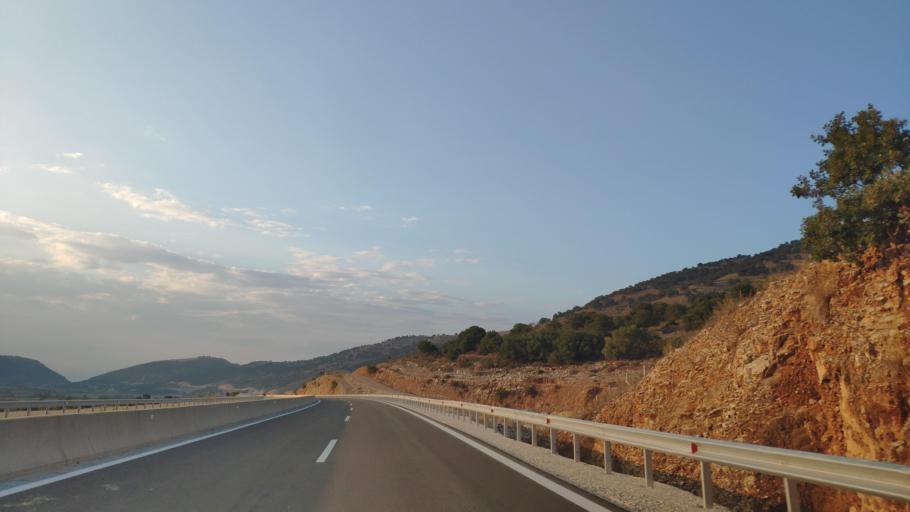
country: GR
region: West Greece
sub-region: Nomos Aitolias kai Akarnanias
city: Katouna
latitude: 38.8057
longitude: 21.1314
